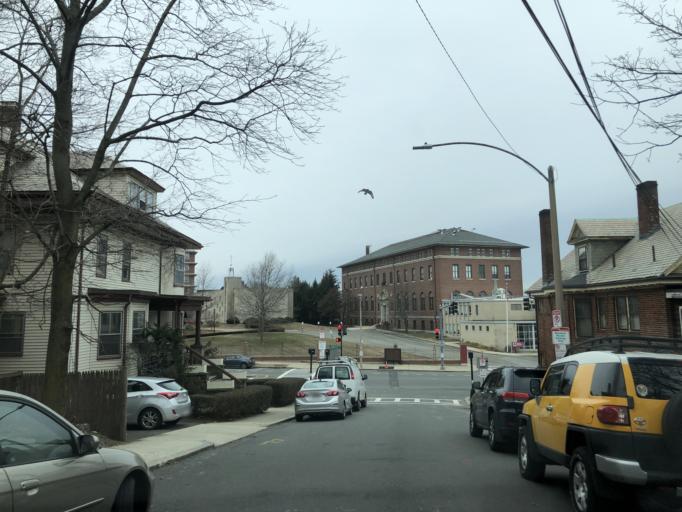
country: US
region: Massachusetts
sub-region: Norfolk County
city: Brookline
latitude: 42.3512
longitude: -71.1429
